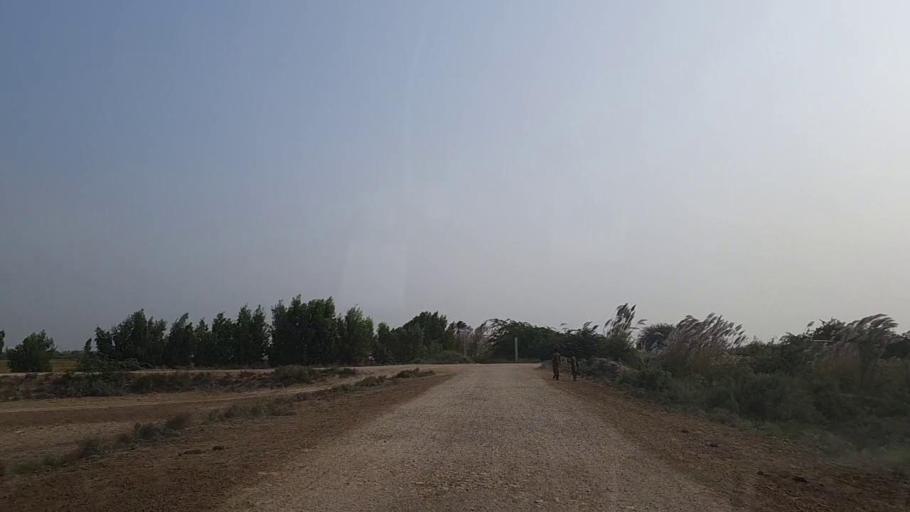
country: PK
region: Sindh
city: Gharo
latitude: 24.6504
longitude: 67.6224
